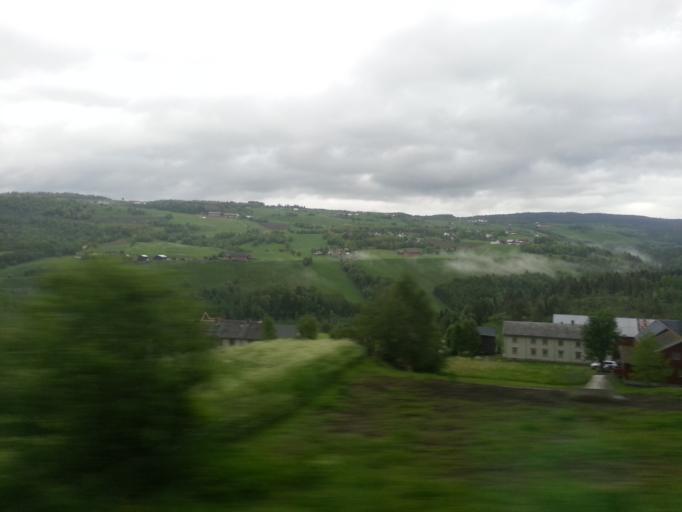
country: NO
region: Sor-Trondelag
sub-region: Midtre Gauldal
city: Storen
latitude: 62.9383
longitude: 10.1831
